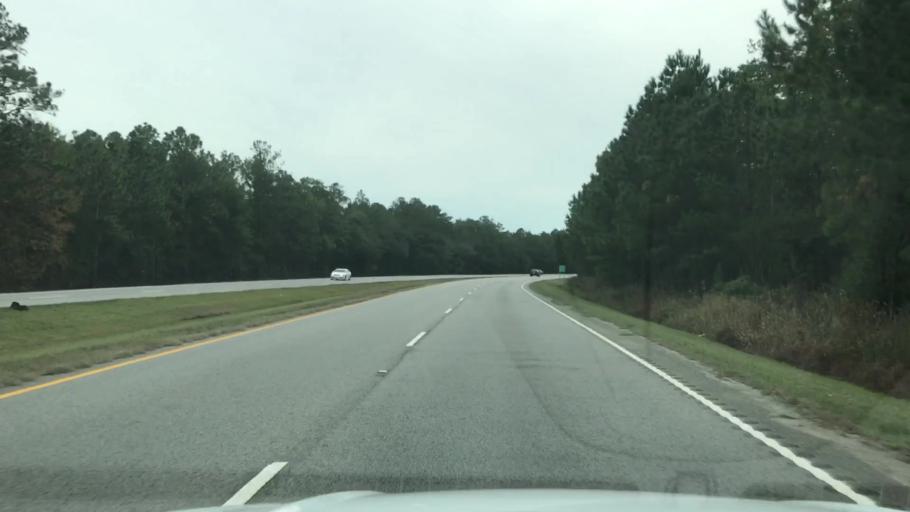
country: US
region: South Carolina
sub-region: Georgetown County
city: Georgetown
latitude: 33.3866
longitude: -79.2051
